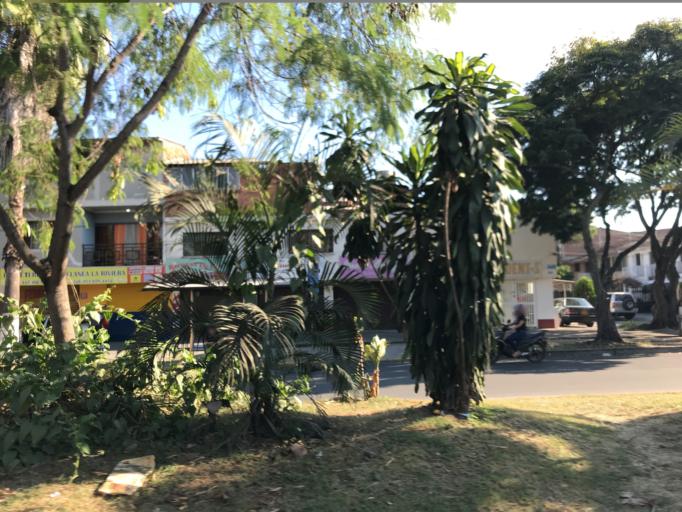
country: CO
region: Valle del Cauca
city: Cali
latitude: 3.4702
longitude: -76.4953
